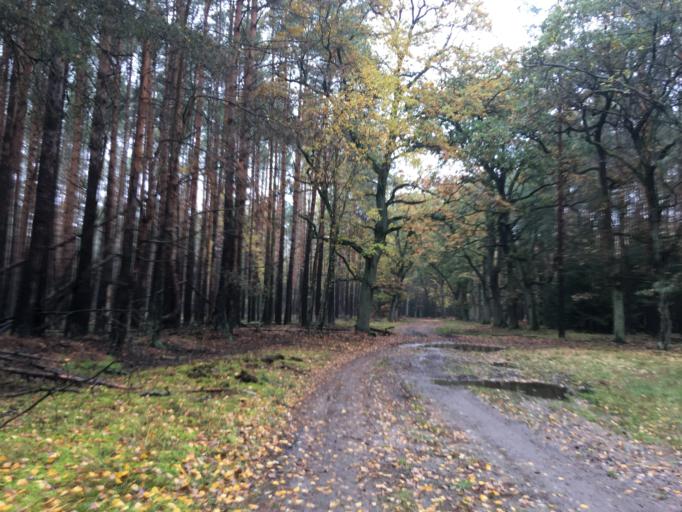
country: DE
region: Brandenburg
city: Beeskow
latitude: 52.2198
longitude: 14.3007
